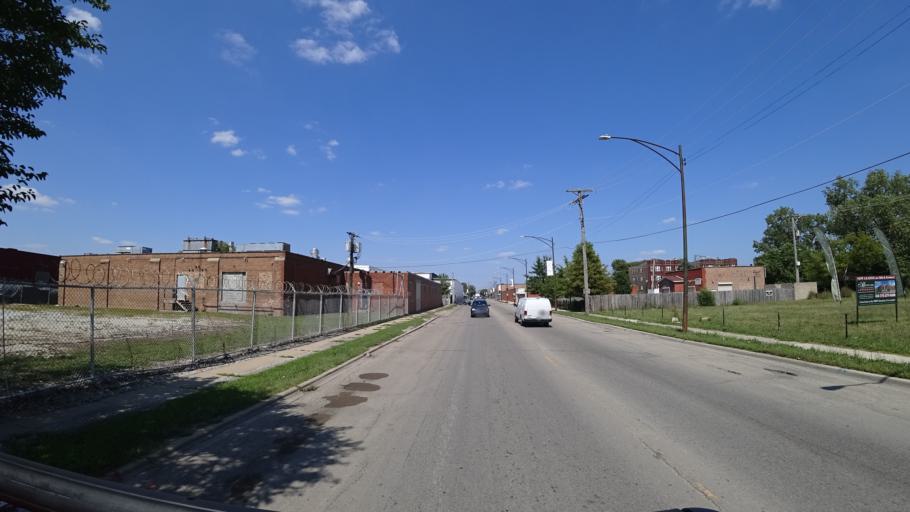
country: US
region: Illinois
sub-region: Cook County
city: Cicero
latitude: 41.8560
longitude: -87.7347
